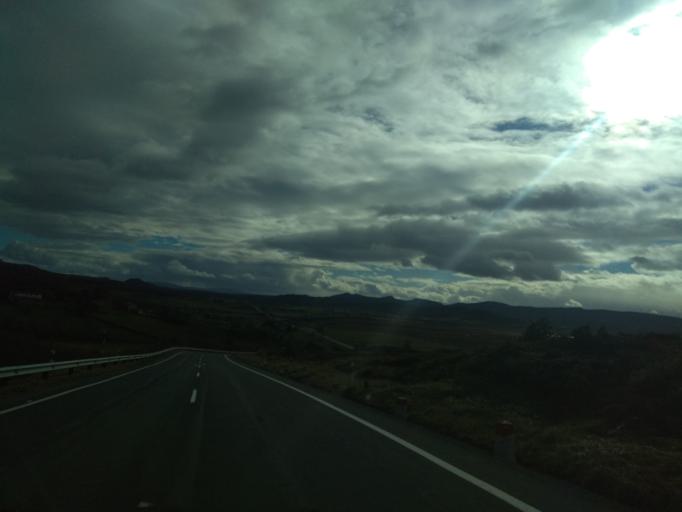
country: ES
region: Castille and Leon
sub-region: Provincia de Burgos
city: Arija
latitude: 43.0326
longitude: -3.8657
